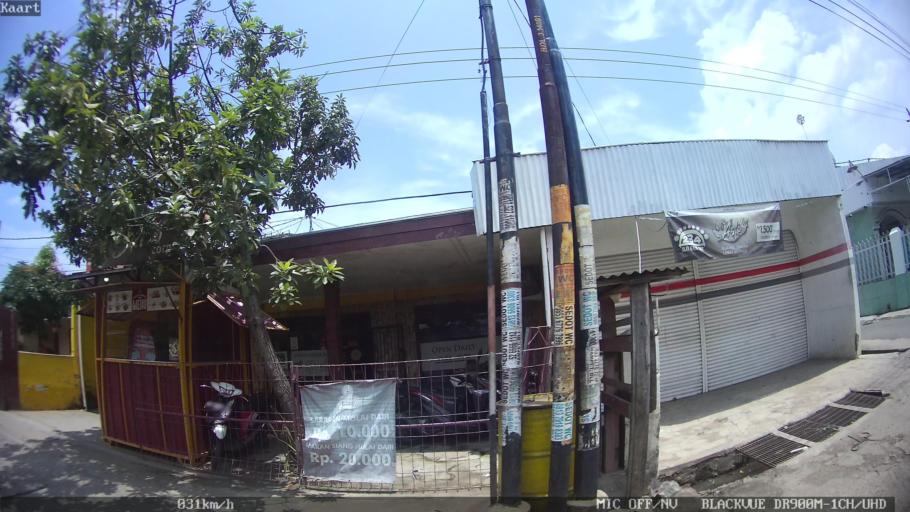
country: ID
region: Lampung
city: Kedaton
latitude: -5.3856
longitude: 105.2531
